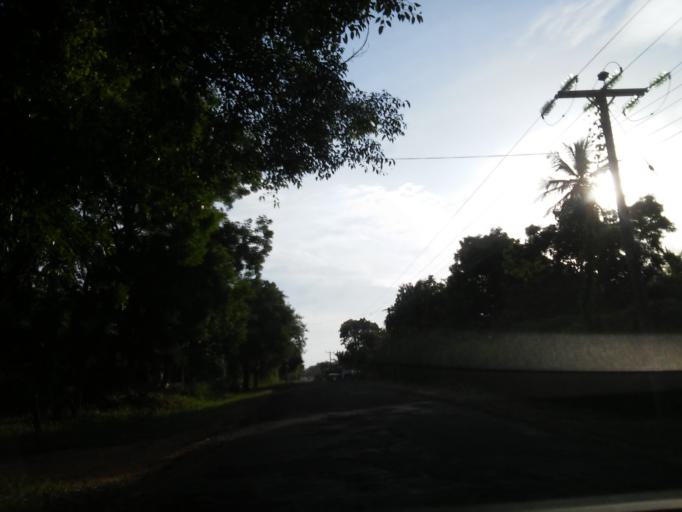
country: LK
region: Central
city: Sigiriya
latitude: 8.1688
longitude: 80.6615
